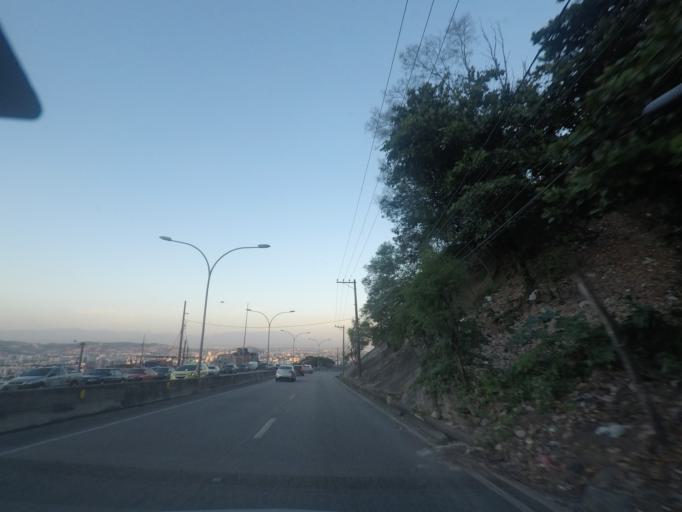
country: BR
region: Rio de Janeiro
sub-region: Rio De Janeiro
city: Rio de Janeiro
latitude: -22.9187
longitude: -43.2839
